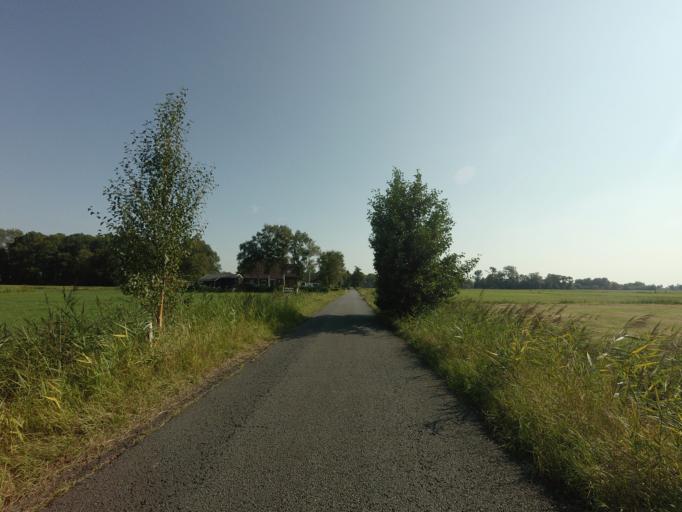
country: NL
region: Groningen
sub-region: Gemeente Zuidhorn
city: Zuidhorn
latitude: 53.2061
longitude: 6.4375
